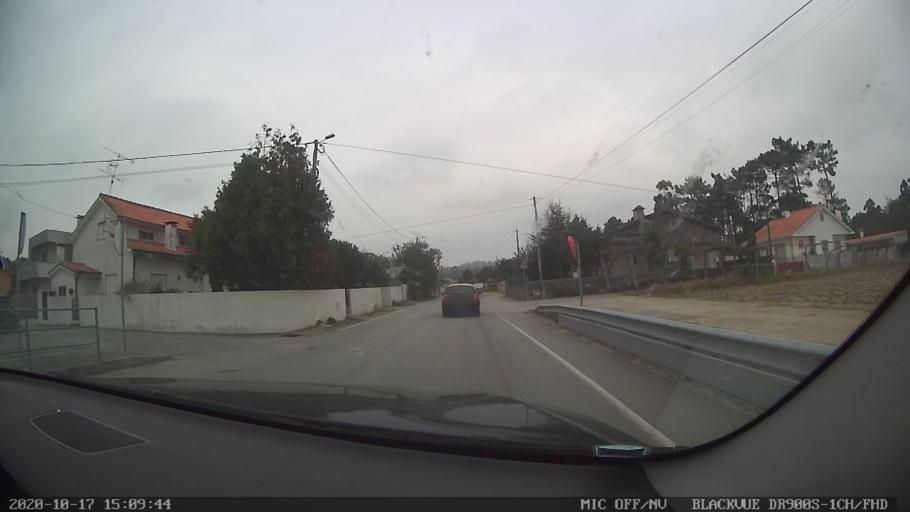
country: PT
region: Braga
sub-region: Esposende
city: Esposende
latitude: 41.5304
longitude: -8.7372
